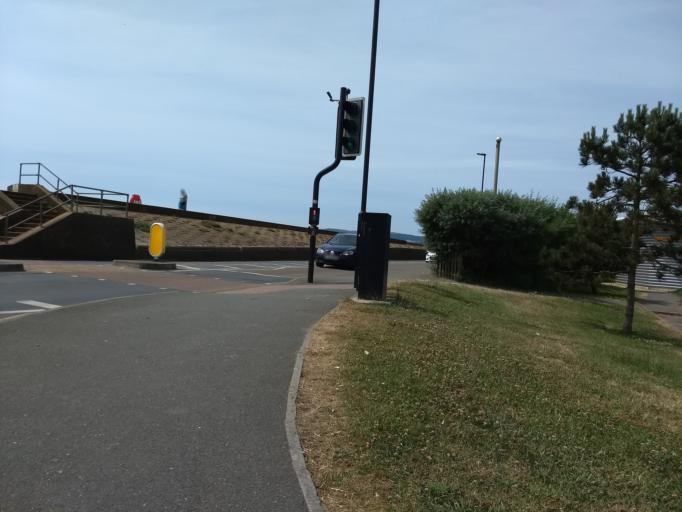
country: GB
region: England
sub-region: Isle of Wight
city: Sandown
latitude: 50.6592
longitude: -1.1421
